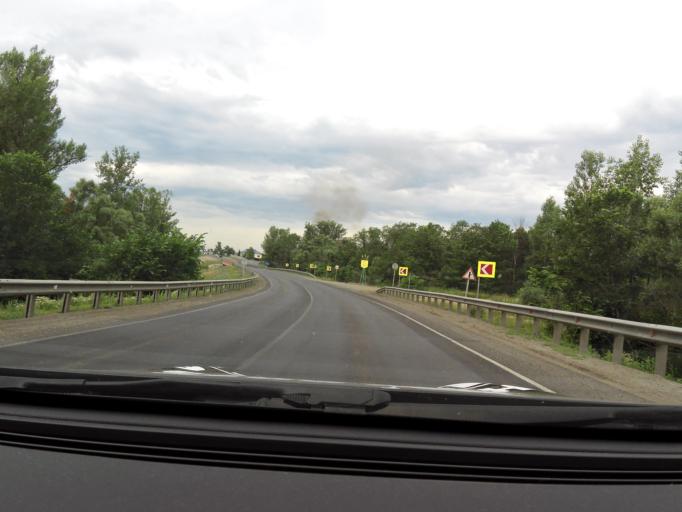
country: RU
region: Bashkortostan
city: Urman
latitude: 54.8267
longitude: 56.8960
